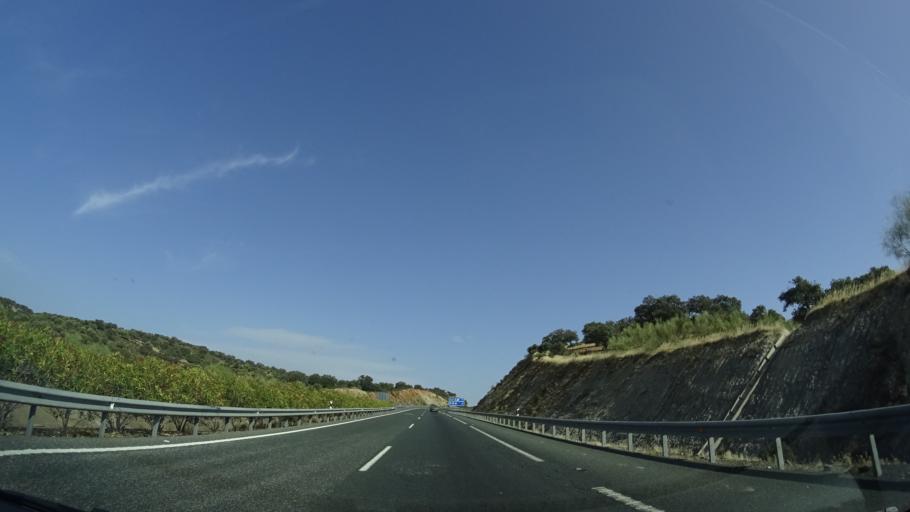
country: ES
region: Andalusia
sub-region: Provincia de Sevilla
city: El Ronquillo
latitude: 37.7049
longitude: -6.1730
